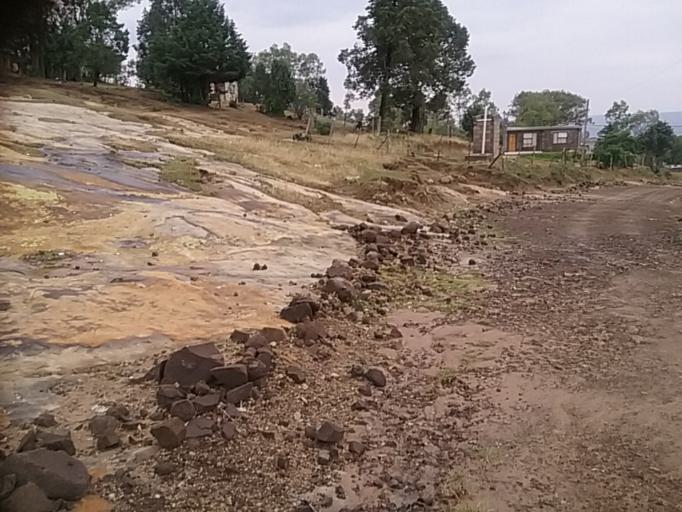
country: LS
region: Berea
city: Teyateyaneng
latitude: -29.1397
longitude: 27.7397
